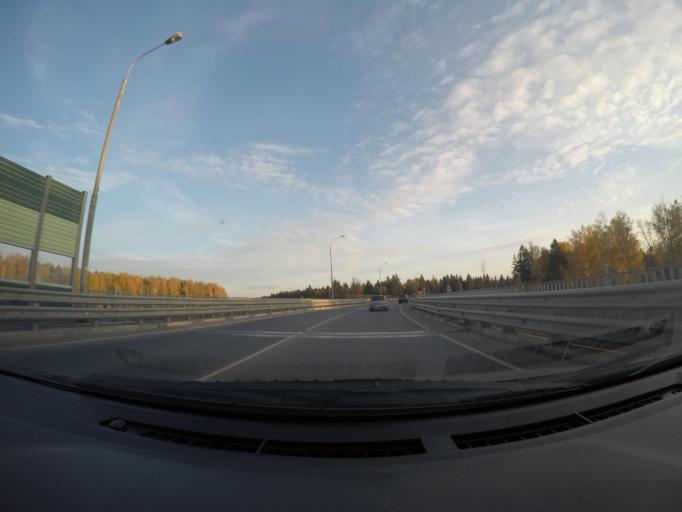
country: RU
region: Moskovskaya
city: Firsanovka
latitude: 55.9587
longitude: 37.2602
